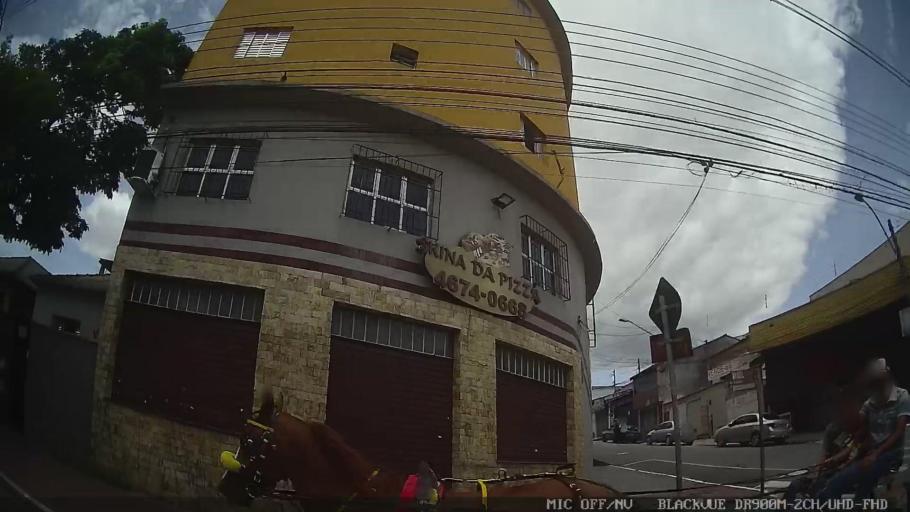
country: BR
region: Sao Paulo
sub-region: Ferraz De Vasconcelos
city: Ferraz de Vasconcelos
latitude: -23.5359
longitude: -46.3578
